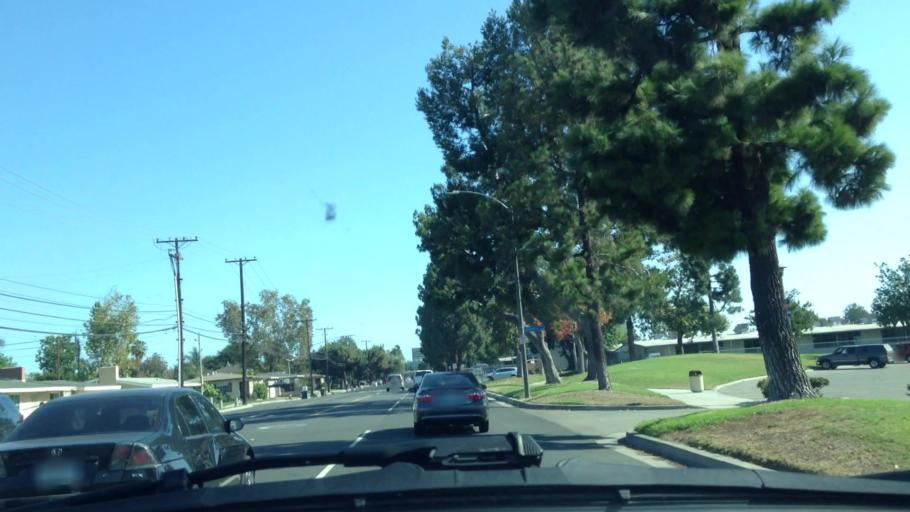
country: US
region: California
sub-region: Orange County
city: Orange
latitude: 33.7940
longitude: -117.8666
